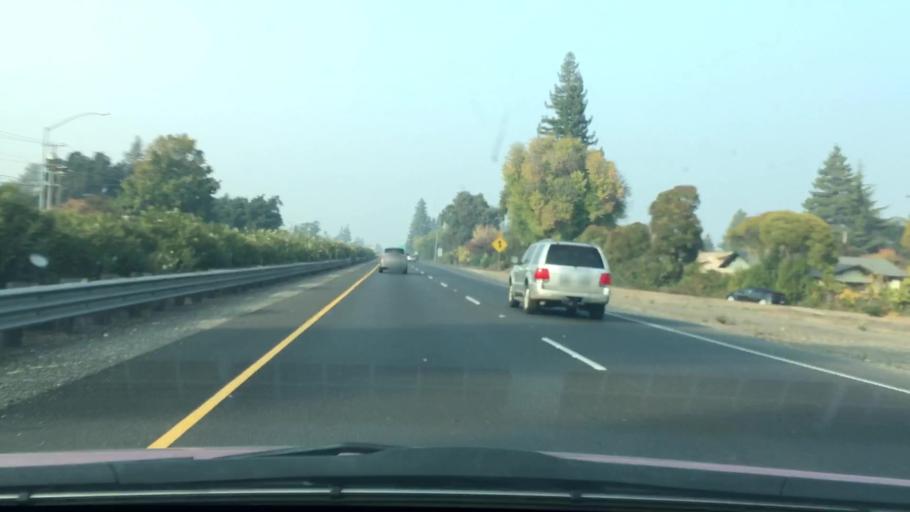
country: US
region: California
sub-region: Napa County
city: Napa
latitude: 38.3075
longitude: -122.3049
